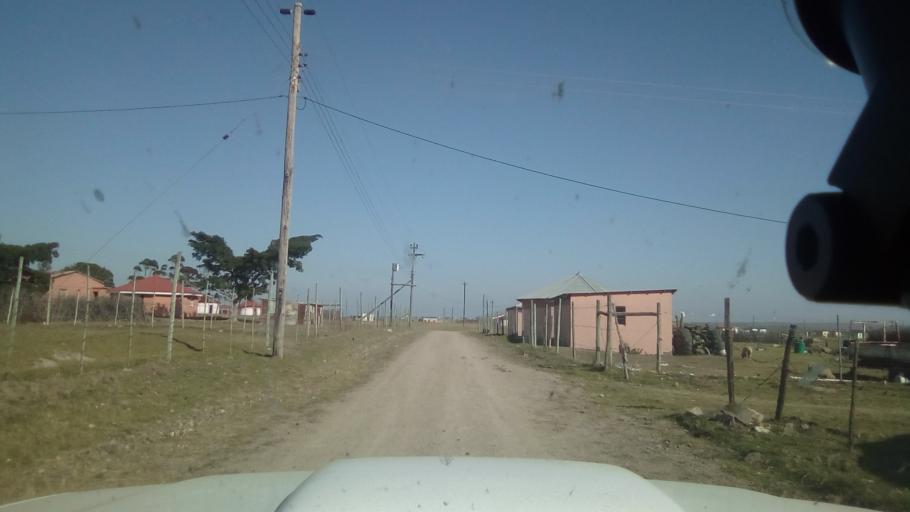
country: ZA
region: Eastern Cape
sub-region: Buffalo City Metropolitan Municipality
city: Bhisho
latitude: -32.9413
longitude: 27.3372
